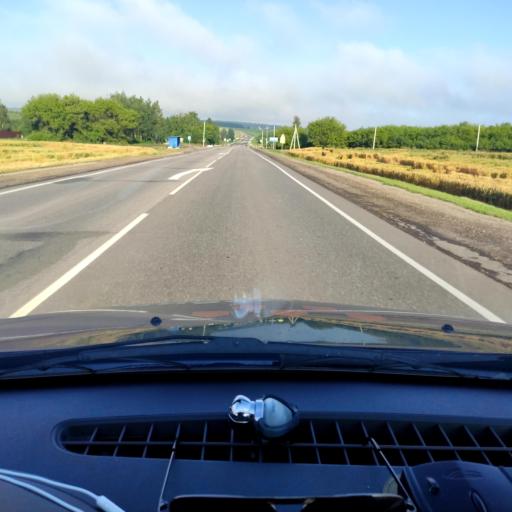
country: RU
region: Orjol
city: Livny
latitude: 52.4479
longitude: 37.4772
